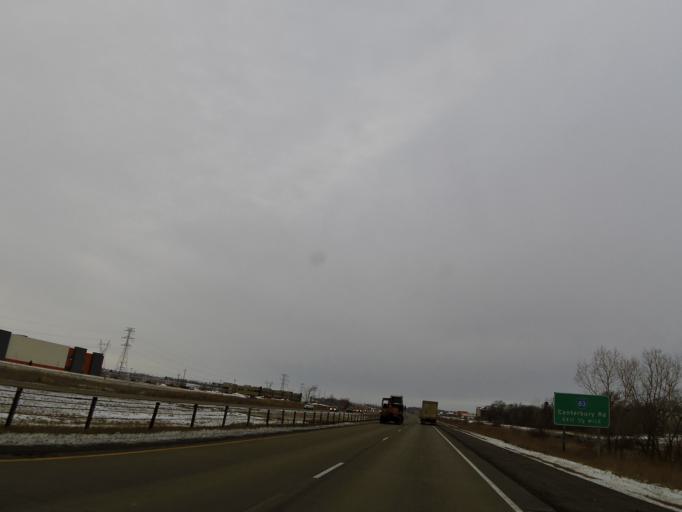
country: US
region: Minnesota
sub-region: Hennepin County
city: Eden Prairie
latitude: 44.7834
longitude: -93.4538
